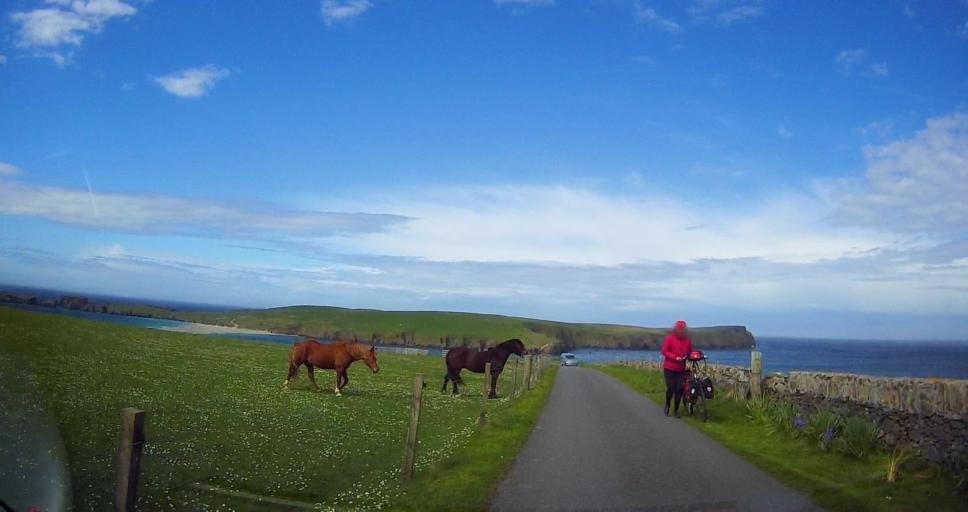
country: GB
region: Scotland
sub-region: Shetland Islands
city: Sandwick
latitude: 59.9731
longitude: -1.3259
